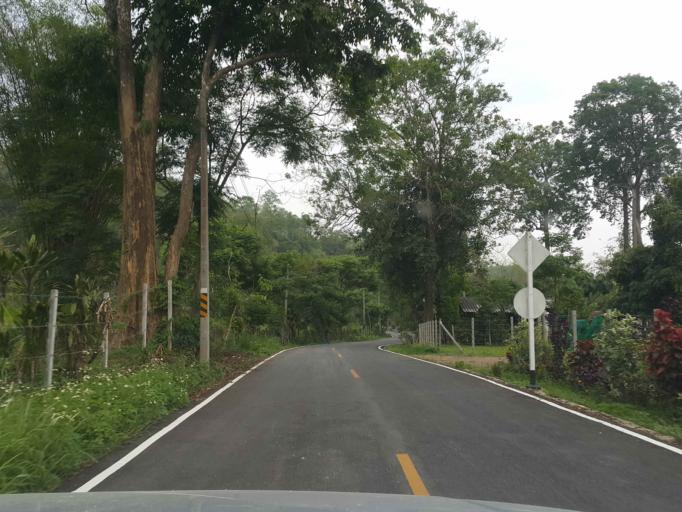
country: TH
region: Chiang Mai
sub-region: Amphoe Chiang Dao
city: Chiang Dao
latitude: 19.4066
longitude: 98.9252
